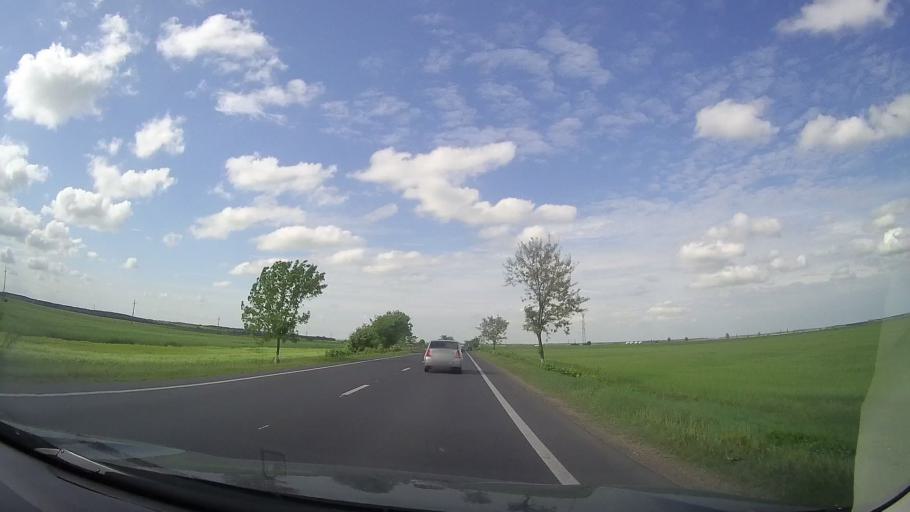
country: RO
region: Giurgiu
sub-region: Comuna Ghimpati
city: Ghimpati
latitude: 44.2171
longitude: 25.8015
